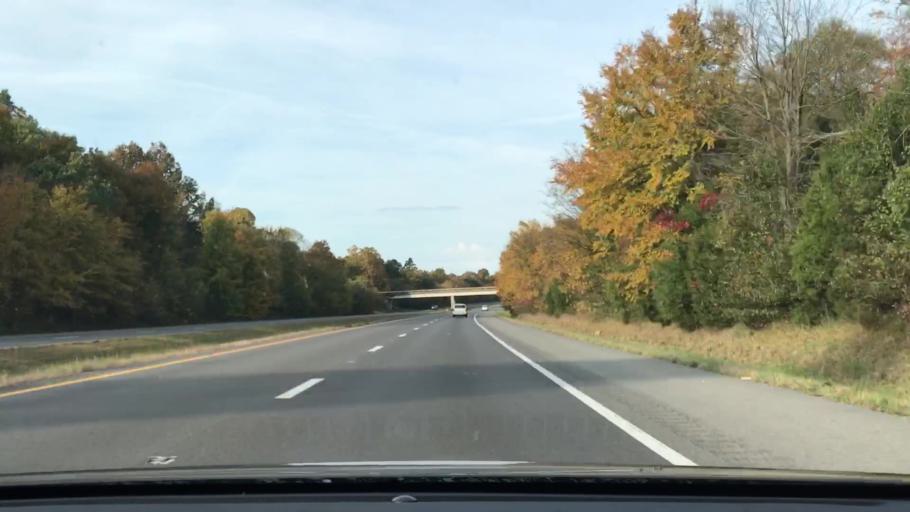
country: US
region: Kentucky
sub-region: Graves County
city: Mayfield
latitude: 36.7715
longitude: -88.6076
